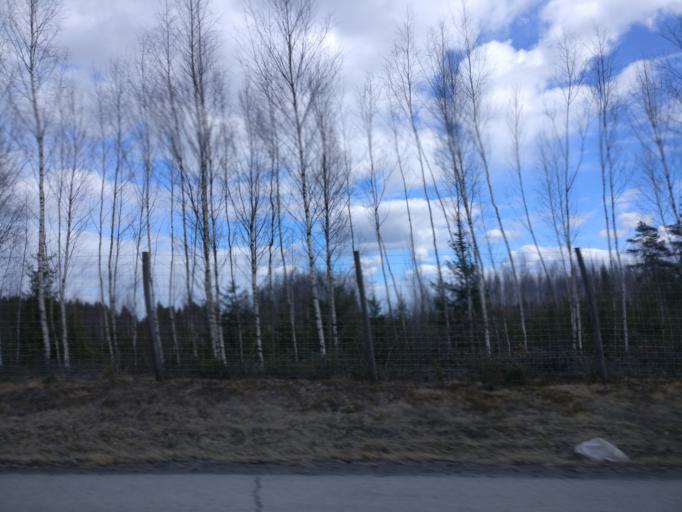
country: FI
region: Haeme
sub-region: Haemeenlinna
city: Tervakoski
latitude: 60.8128
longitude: 24.6772
